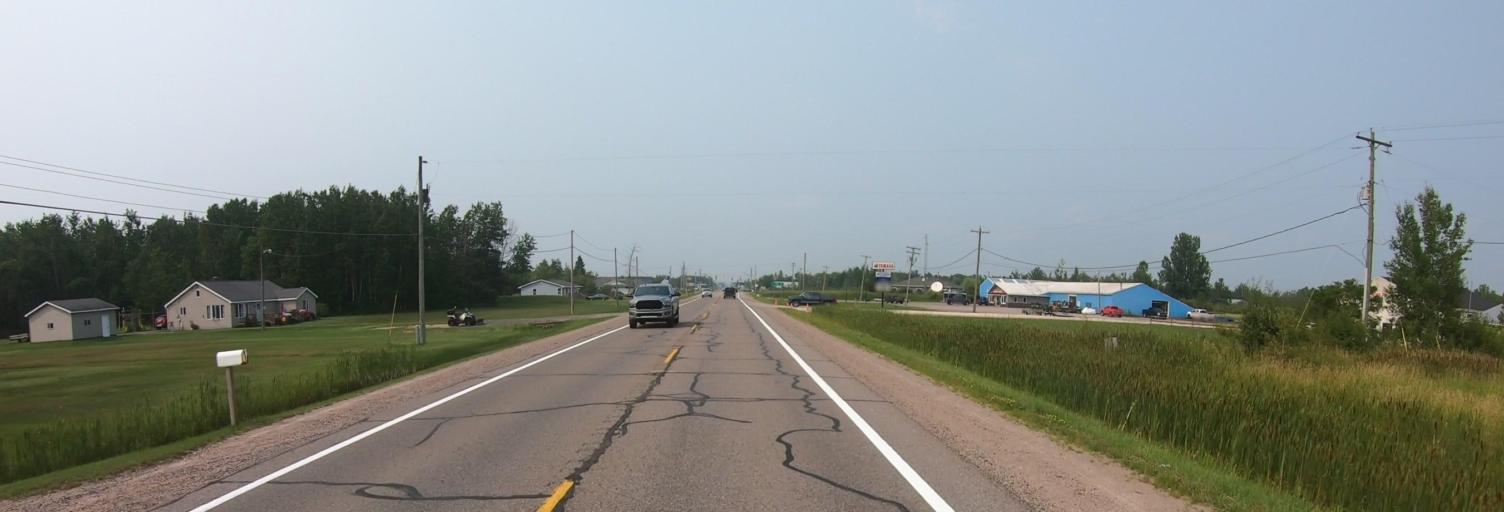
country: US
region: Michigan
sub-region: Chippewa County
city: Sault Ste. Marie
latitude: 46.4597
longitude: -84.3542
